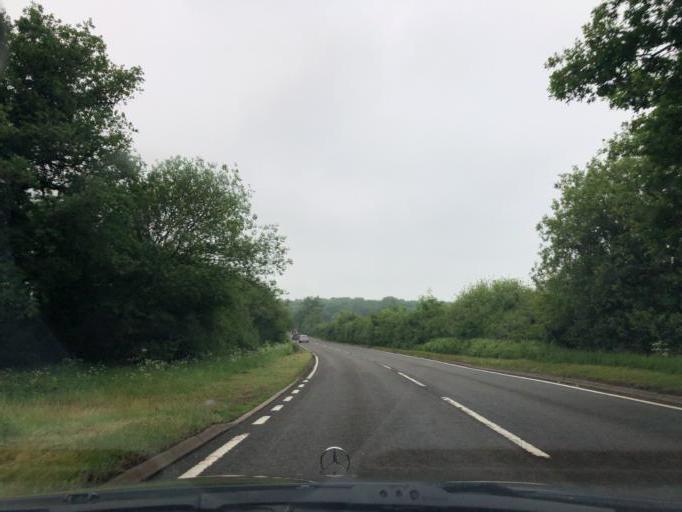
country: GB
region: England
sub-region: Warwickshire
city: Harbury
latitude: 52.2063
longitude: -1.4920
